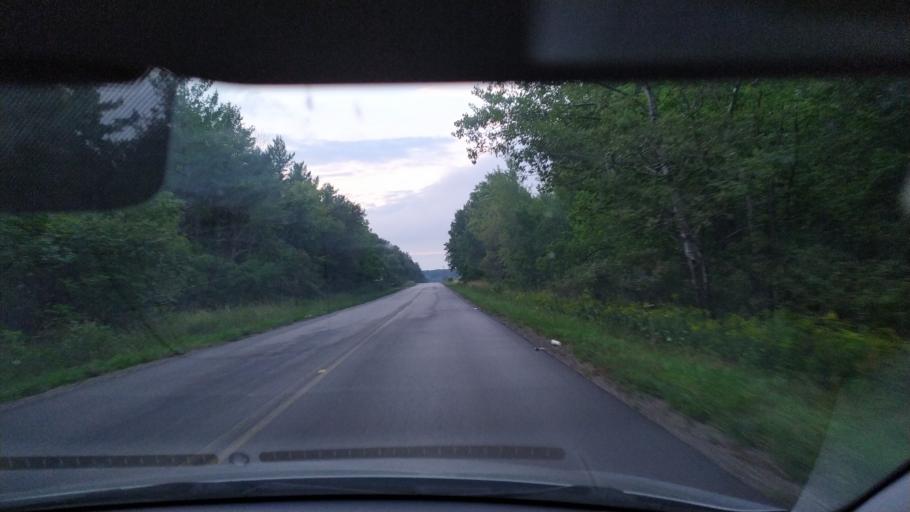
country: CA
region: Ontario
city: Kitchener
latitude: 43.3508
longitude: -80.6430
